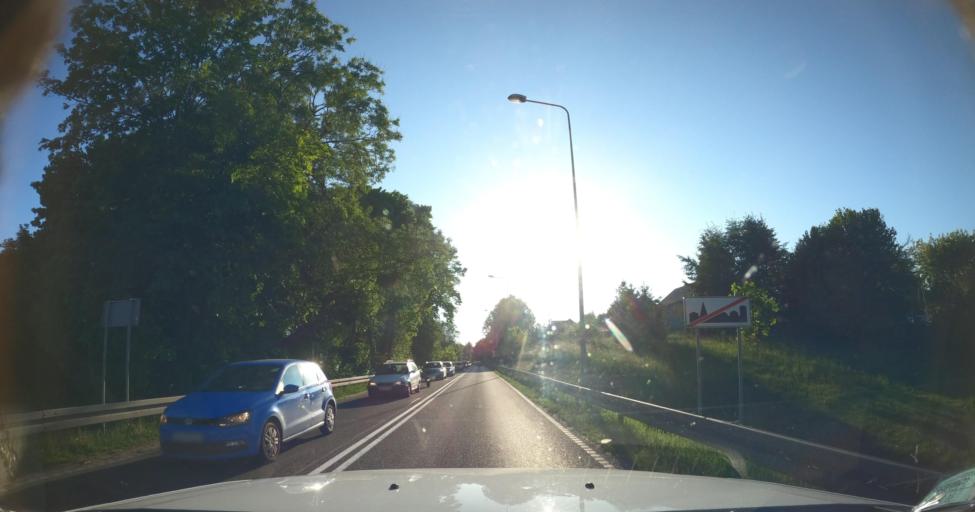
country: PL
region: Pomeranian Voivodeship
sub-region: Powiat kartuski
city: Zukowo
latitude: 54.3401
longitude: 18.3504
